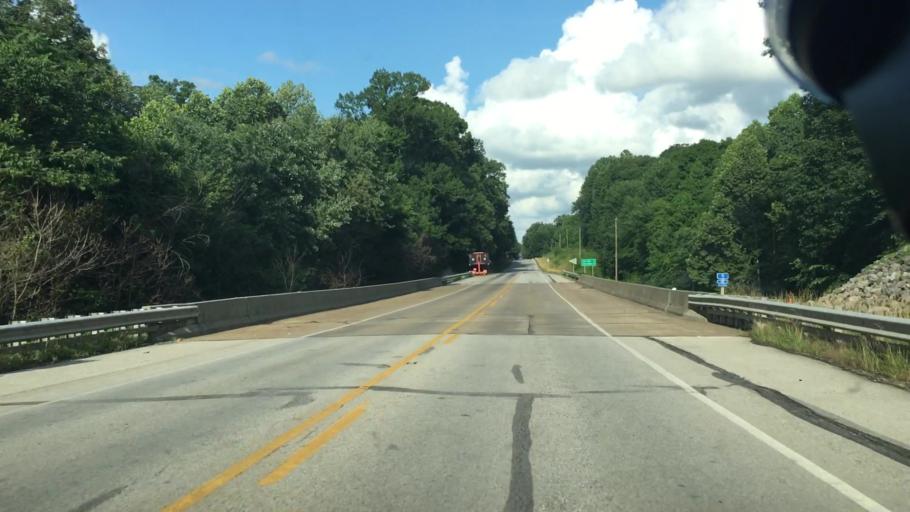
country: US
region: Kentucky
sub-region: Hancock County
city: Lewisport
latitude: 38.0014
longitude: -86.8552
